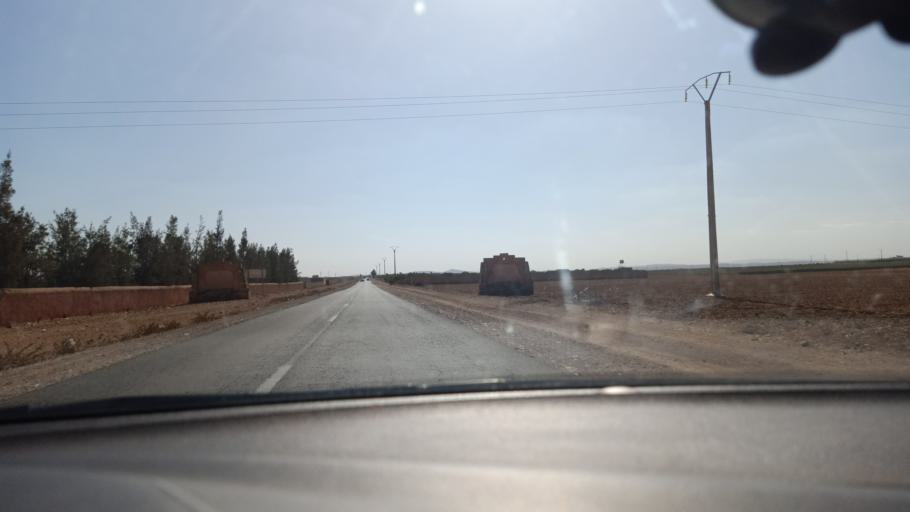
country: MA
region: Doukkala-Abda
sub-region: Safi
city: Youssoufia
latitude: 32.1303
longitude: -8.5996
